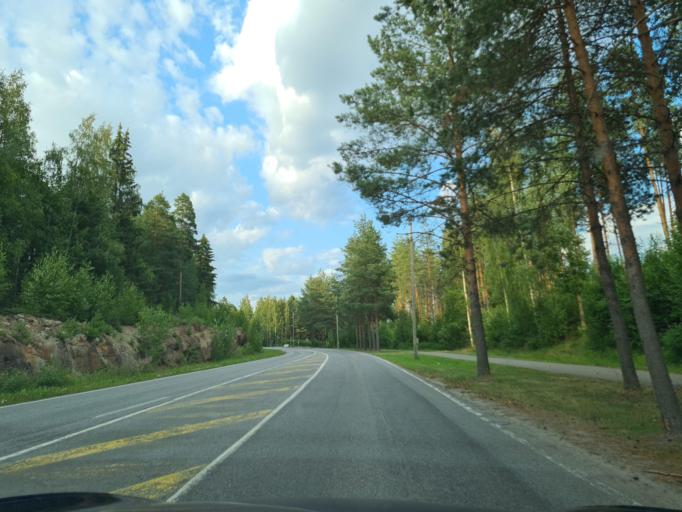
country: FI
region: Southern Ostrobothnia
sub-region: Seinaejoki
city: Lapua
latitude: 62.9797
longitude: 23.0424
